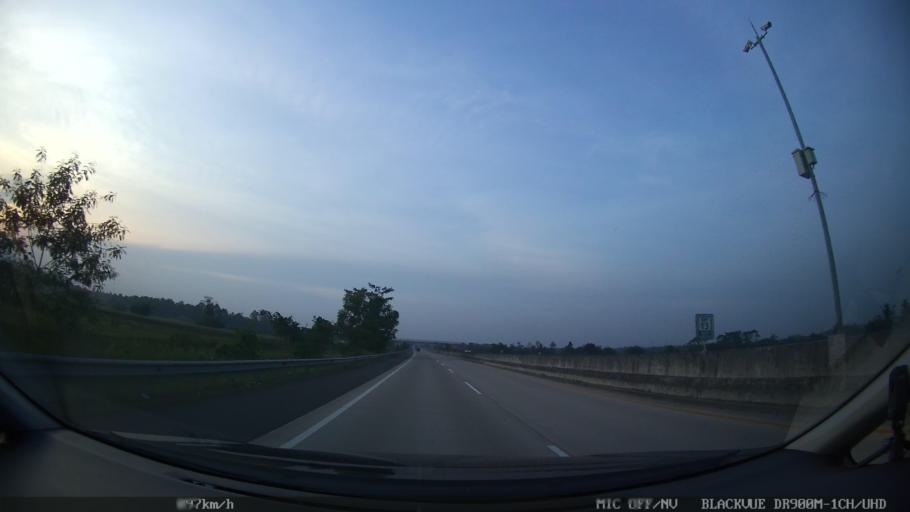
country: ID
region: Lampung
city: Penengahan
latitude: -5.7647
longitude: 105.7138
